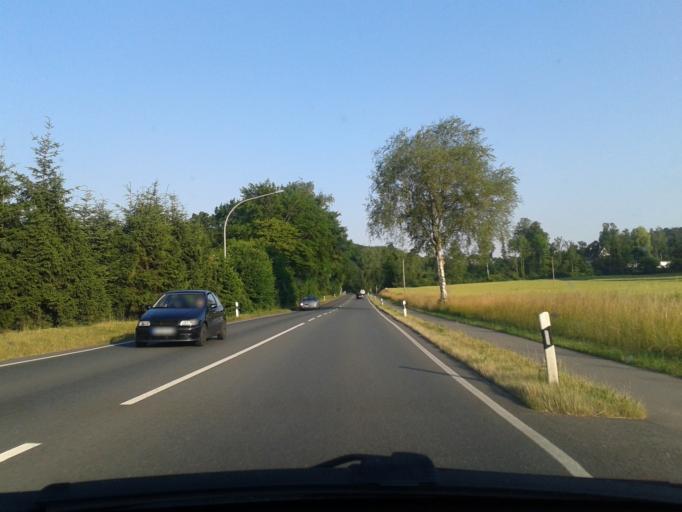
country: DE
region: North Rhine-Westphalia
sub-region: Regierungsbezirk Detmold
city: Horn
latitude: 51.9086
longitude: 8.9239
